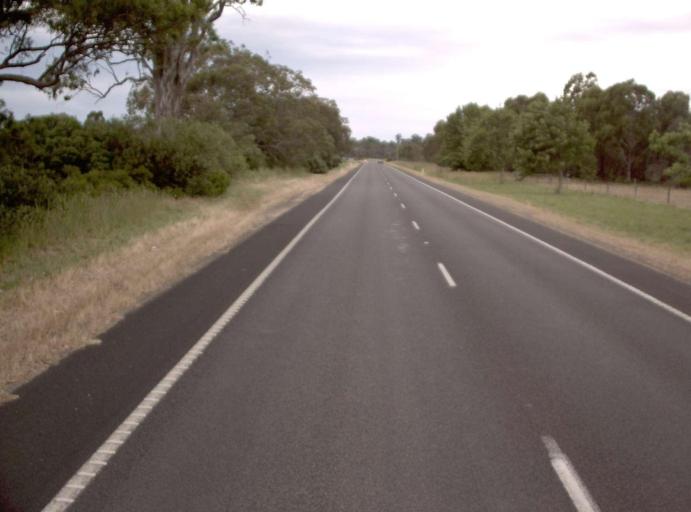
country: AU
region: Victoria
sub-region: East Gippsland
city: Bairnsdale
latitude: -37.8771
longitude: 147.6540
